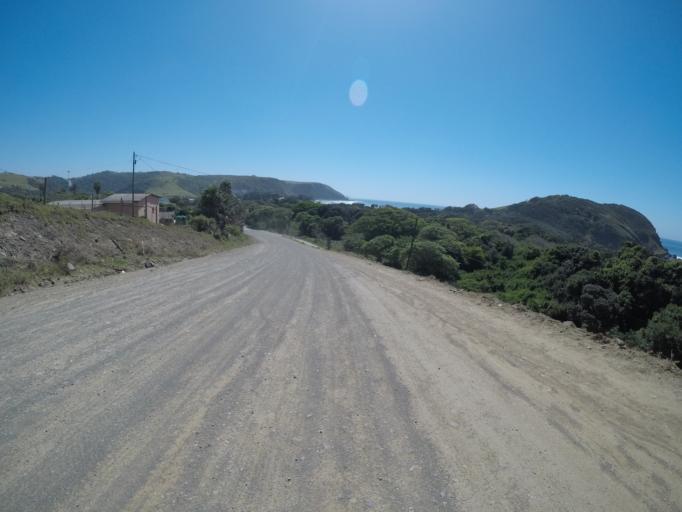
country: ZA
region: Eastern Cape
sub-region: OR Tambo District Municipality
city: Libode
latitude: -31.9870
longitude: 29.1476
